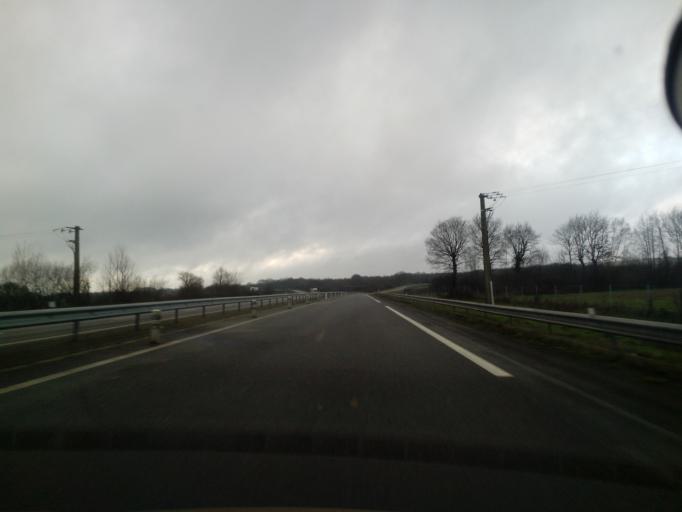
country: FR
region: Brittany
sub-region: Departement des Cotes-d'Armor
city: Merdrignac
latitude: 48.1921
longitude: -2.3248
